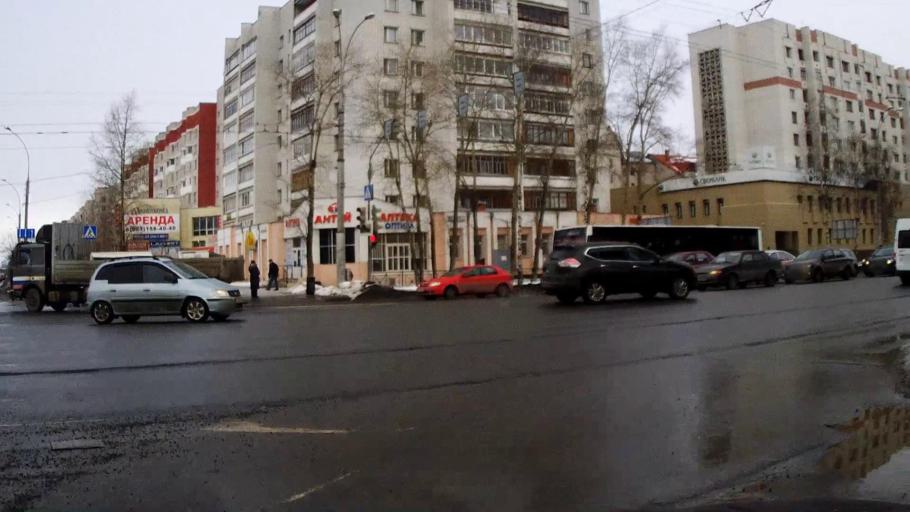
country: RU
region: Vologda
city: Vologda
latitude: 59.2127
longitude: 39.8515
